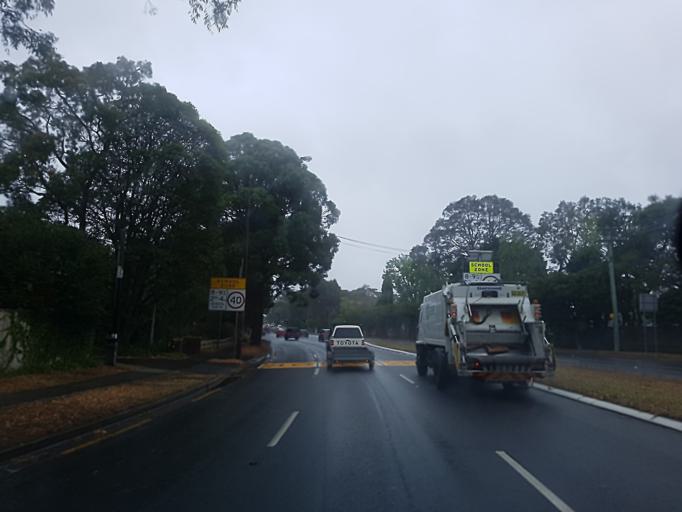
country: AU
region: New South Wales
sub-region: City of Sydney
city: North Turramurra
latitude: -33.7232
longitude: 151.1709
